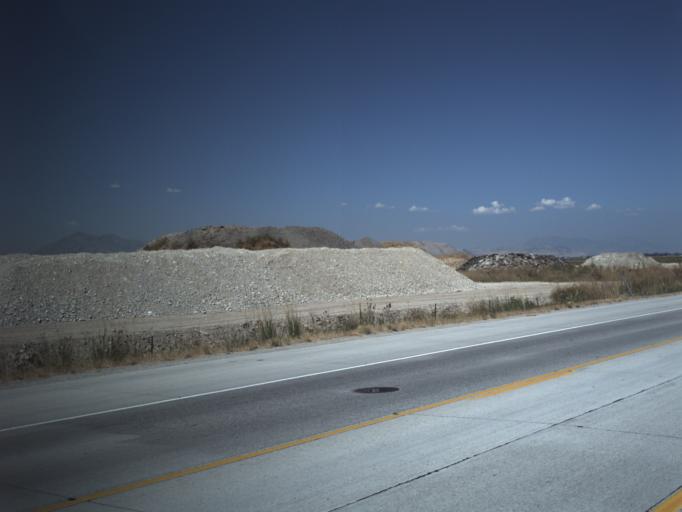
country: US
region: Utah
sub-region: Cache County
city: Logan
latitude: 41.7712
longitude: -111.8585
